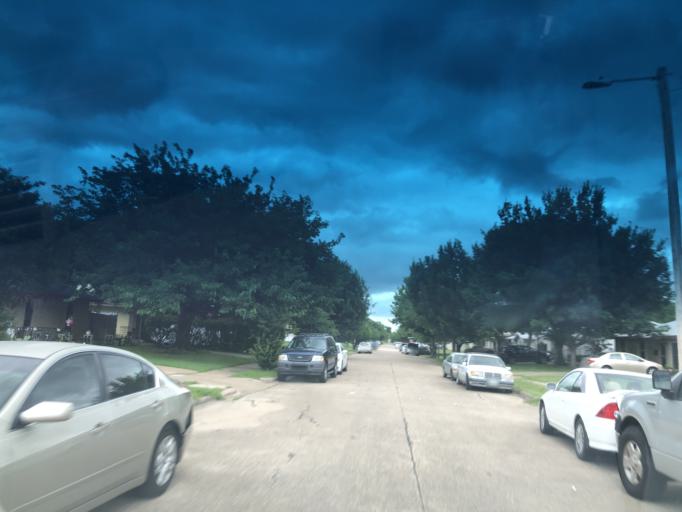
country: US
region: Texas
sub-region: Dallas County
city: Grand Prairie
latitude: 32.7026
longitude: -97.0134
